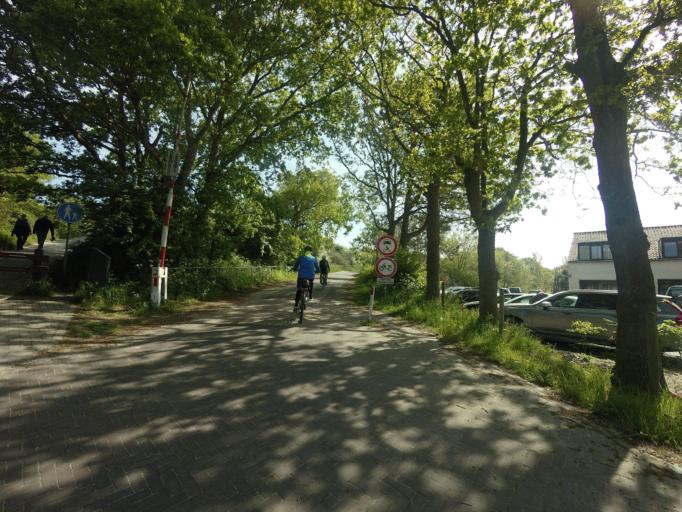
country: NL
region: Zeeland
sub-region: Gemeente Veere
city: Veere
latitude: 51.5863
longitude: 3.6209
